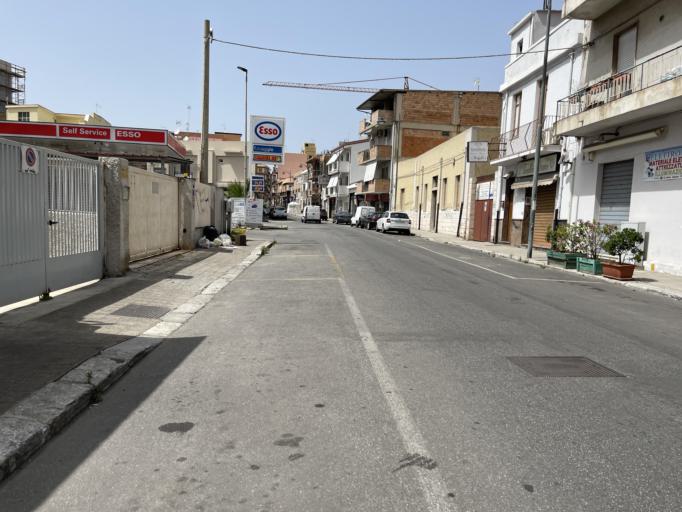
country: IT
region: Calabria
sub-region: Provincia di Reggio Calabria
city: Reggio Calabria
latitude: 38.0994
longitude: 15.6428
